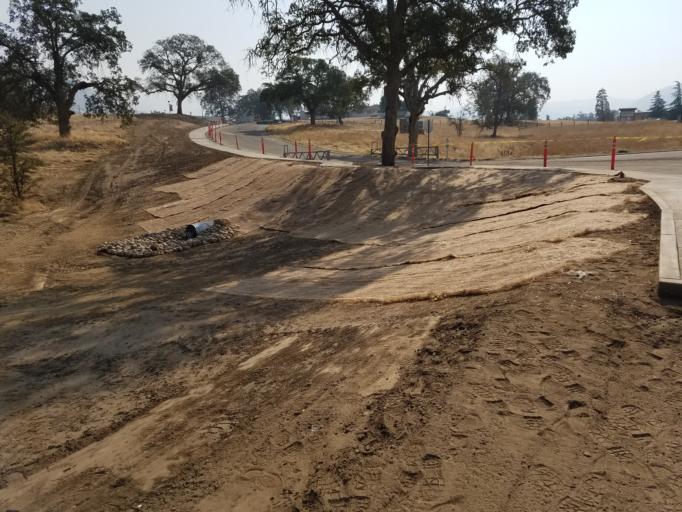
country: US
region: California
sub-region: Fresno County
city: Squaw Valley
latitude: 36.7355
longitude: -119.1185
